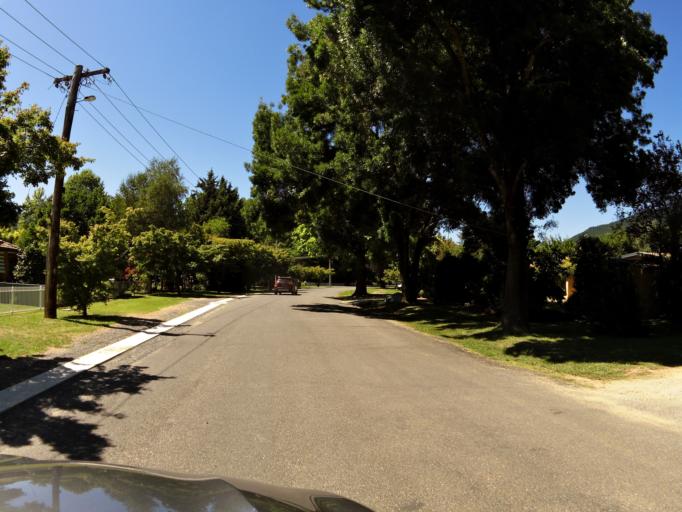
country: AU
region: Victoria
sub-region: Alpine
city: Mount Beauty
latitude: -36.7341
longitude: 146.9682
